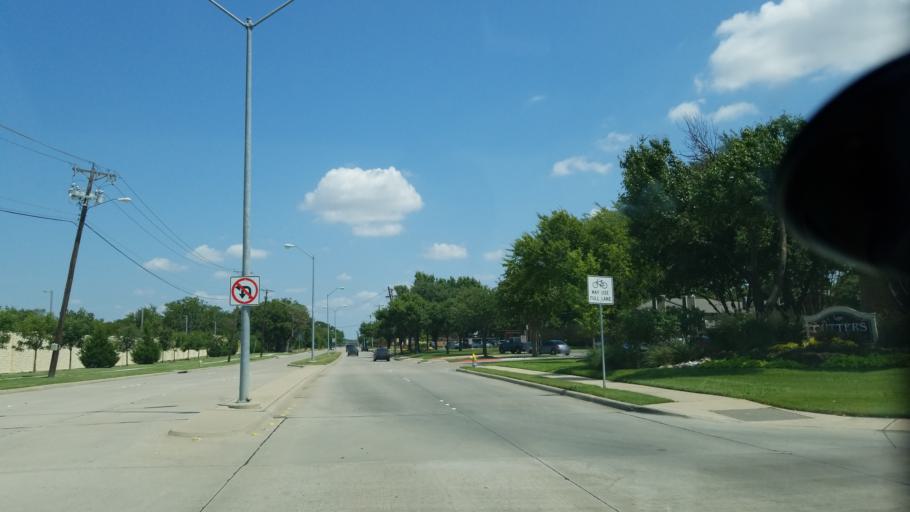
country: US
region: Texas
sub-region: Dallas County
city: Richardson
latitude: 32.9272
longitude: -96.7354
